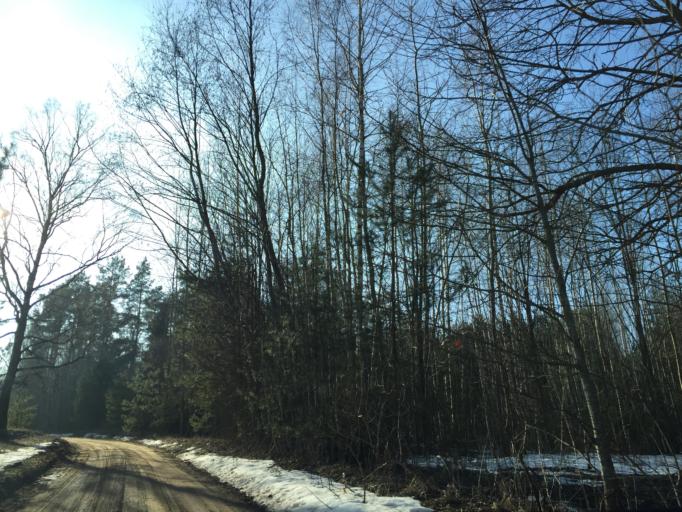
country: LV
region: Lecava
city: Iecava
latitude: 56.6790
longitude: 24.1991
